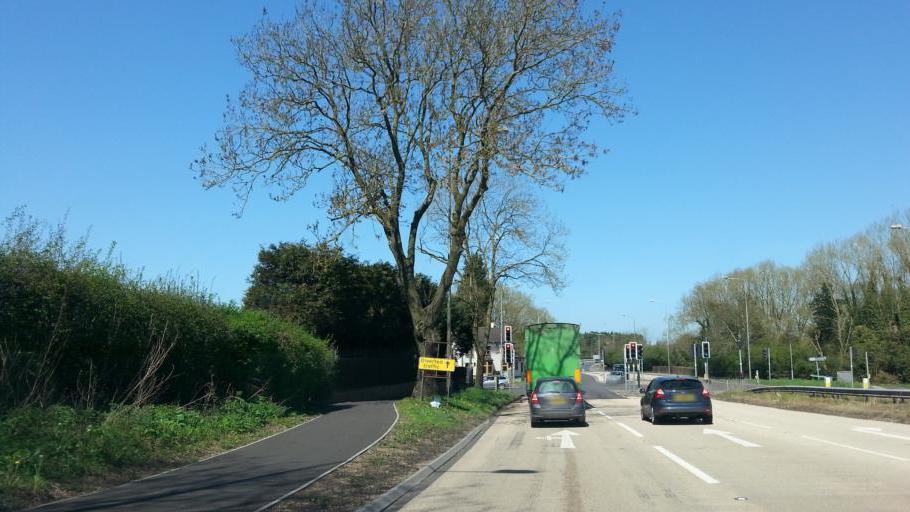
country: GB
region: England
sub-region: Staffordshire
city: Brewood
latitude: 52.6664
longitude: -2.1317
